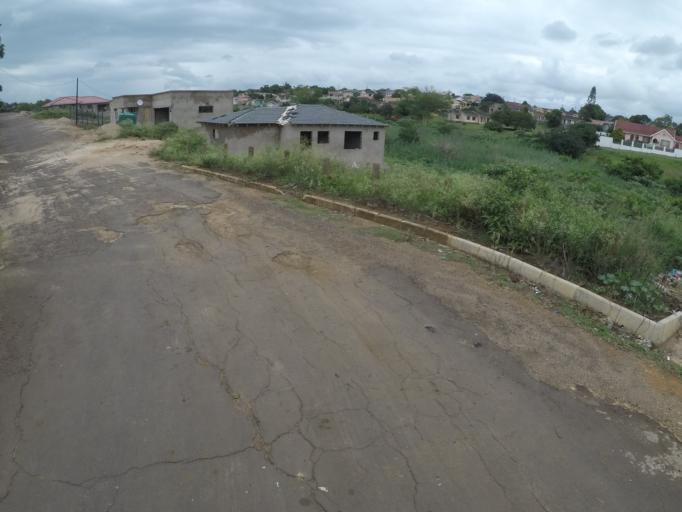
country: ZA
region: KwaZulu-Natal
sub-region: uThungulu District Municipality
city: Empangeni
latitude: -28.7795
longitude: 31.8573
